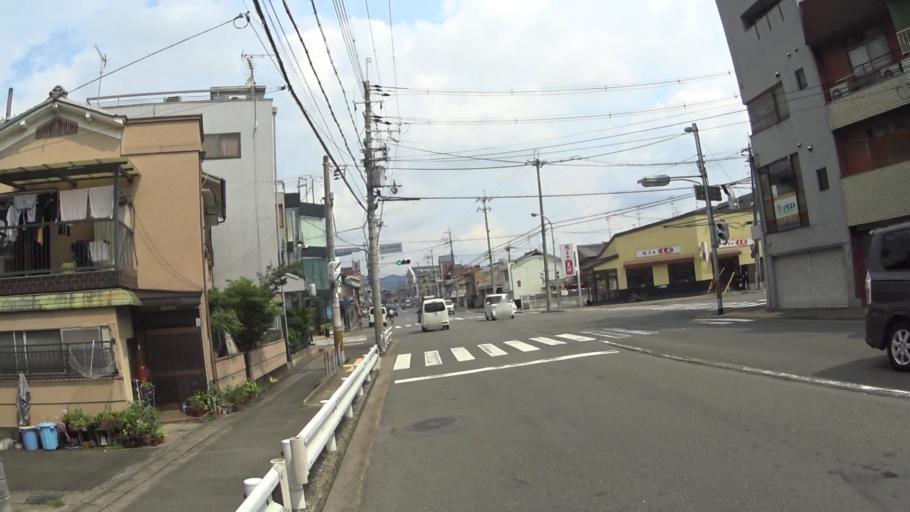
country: JP
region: Kyoto
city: Muko
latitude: 35.0009
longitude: 135.7053
